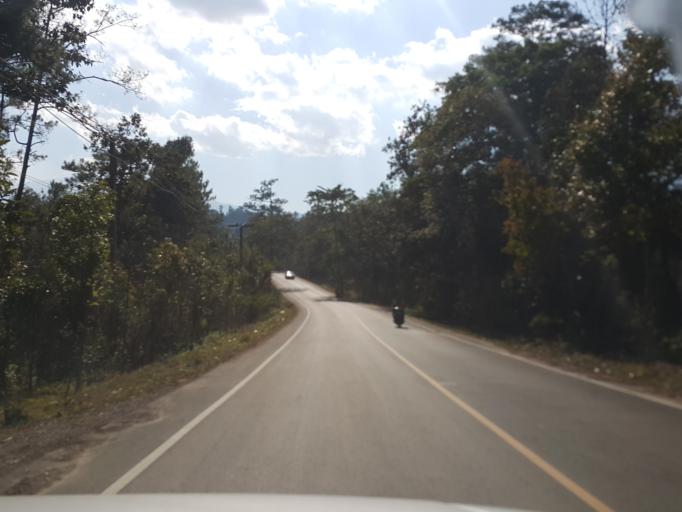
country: TH
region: Chiang Mai
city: Mae Wang
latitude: 18.6954
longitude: 98.5671
